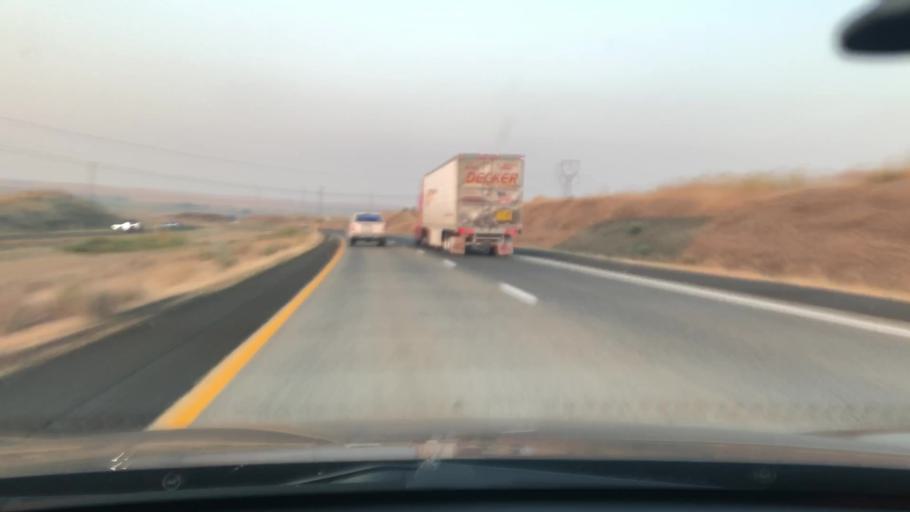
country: US
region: Washington
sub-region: Franklin County
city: Connell
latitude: 46.6396
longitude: -118.8626
